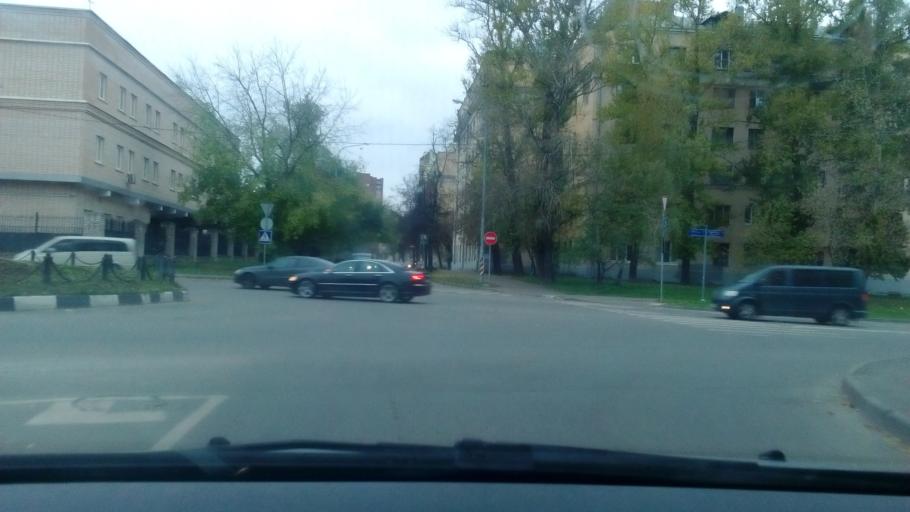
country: RU
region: Moscow
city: Sokol
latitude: 55.7980
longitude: 37.5537
